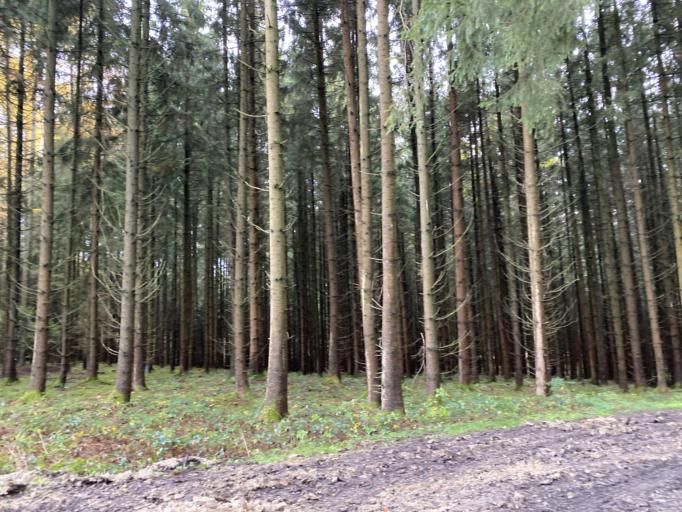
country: DE
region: Bavaria
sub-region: Upper Bavaria
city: Wolfersdorf
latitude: 48.5013
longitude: 11.7117
